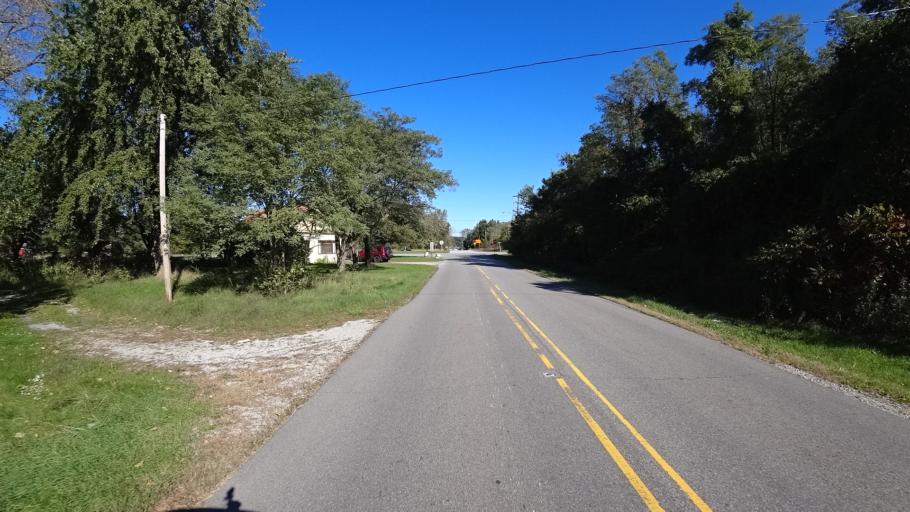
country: US
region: Indiana
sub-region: LaPorte County
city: Michigan City
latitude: 41.6949
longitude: -86.9324
